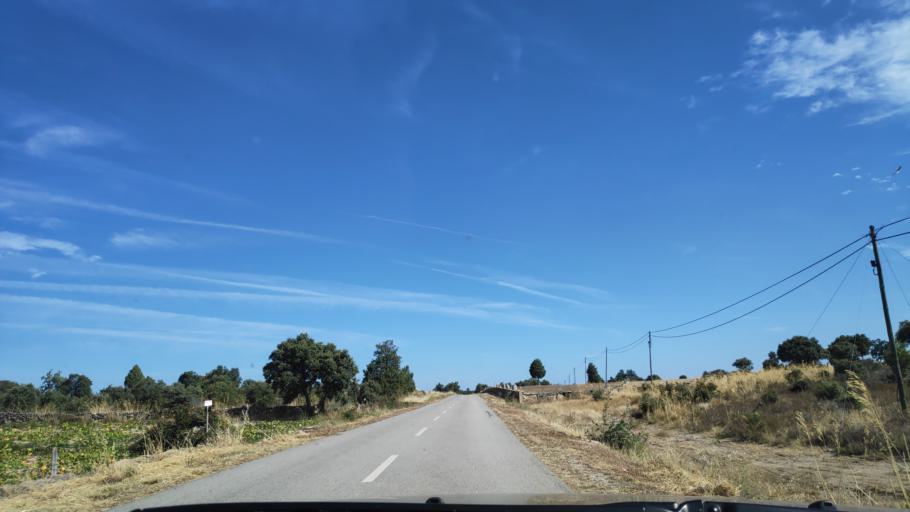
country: PT
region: Braganca
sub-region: Miranda do Douro
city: Miranda do Douro
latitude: 41.4516
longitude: -6.3551
